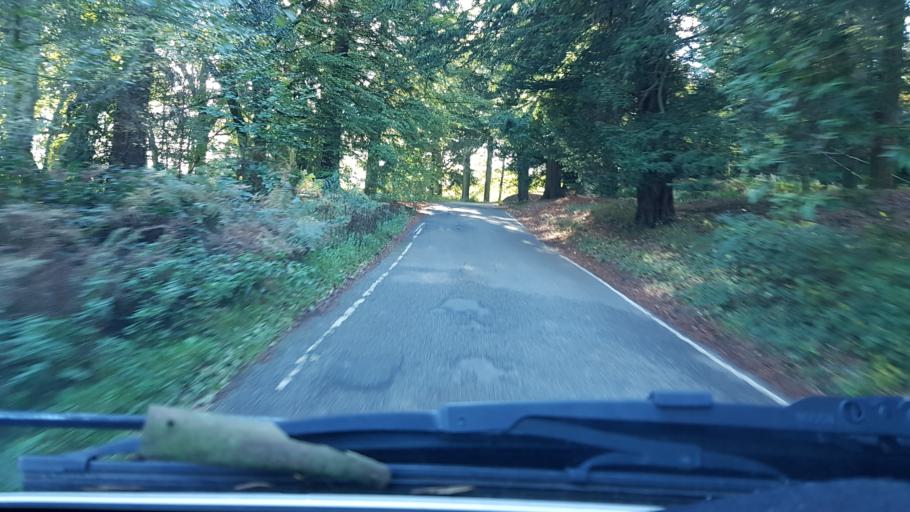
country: GB
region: England
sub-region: Surrey
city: Ockley
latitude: 51.1761
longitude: -0.3633
